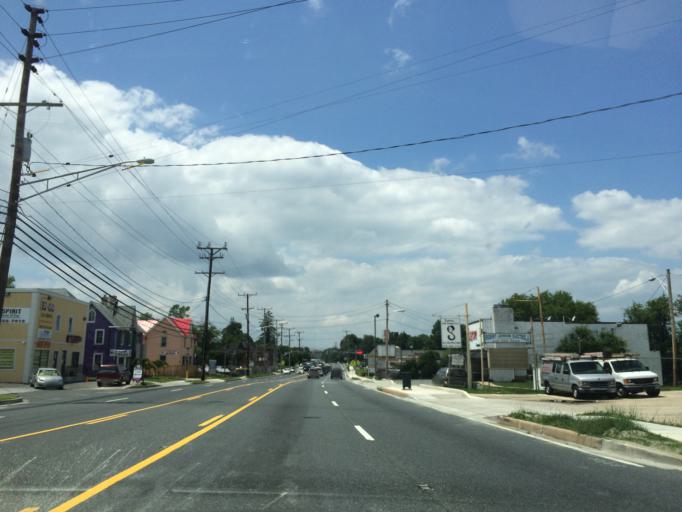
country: US
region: Maryland
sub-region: Baltimore County
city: Randallstown
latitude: 39.3681
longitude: -76.7971
